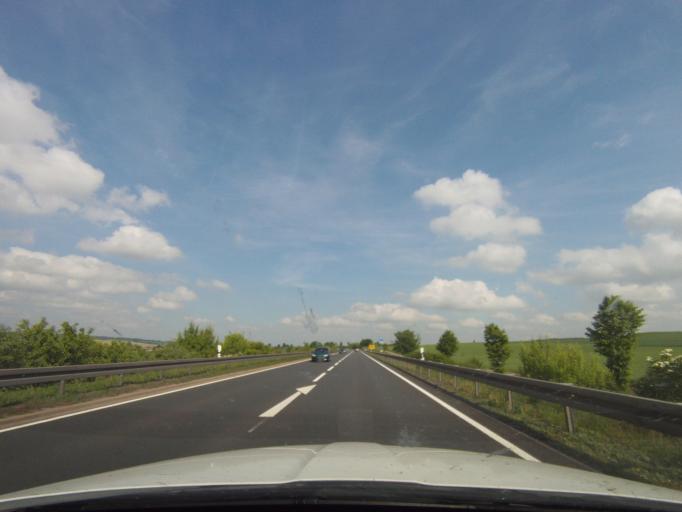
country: DE
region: Thuringia
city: Dreitzsch
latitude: 50.7355
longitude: 11.7934
